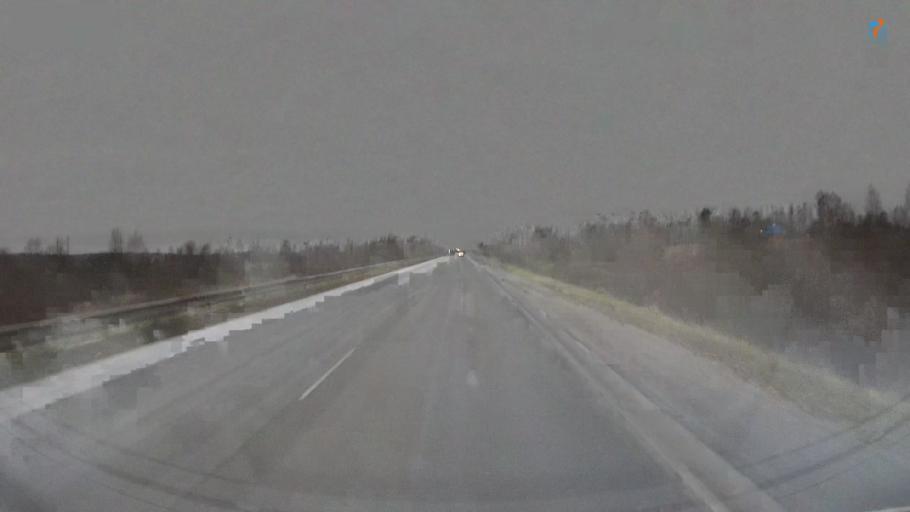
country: RU
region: Vologda
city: Cherepovets
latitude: 59.0244
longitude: 38.0269
